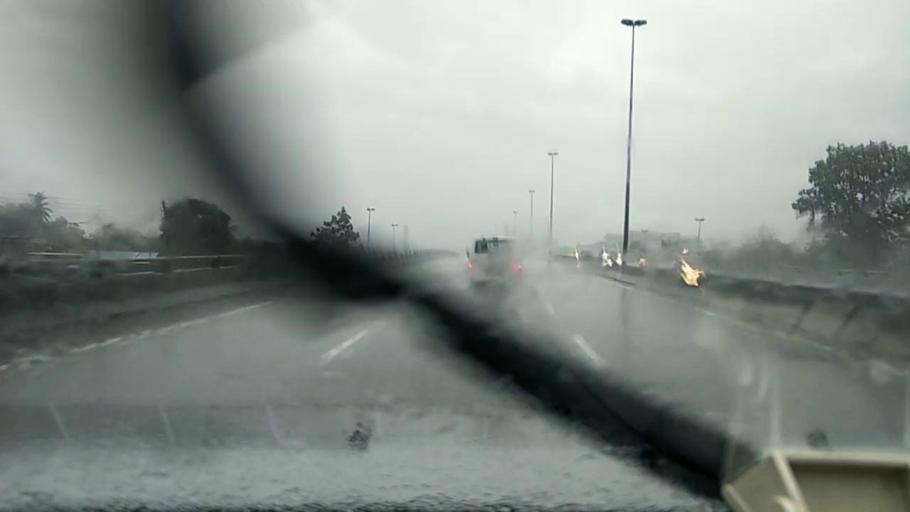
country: MY
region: Selangor
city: Kampong Baharu Balakong
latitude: 2.9847
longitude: 101.7650
